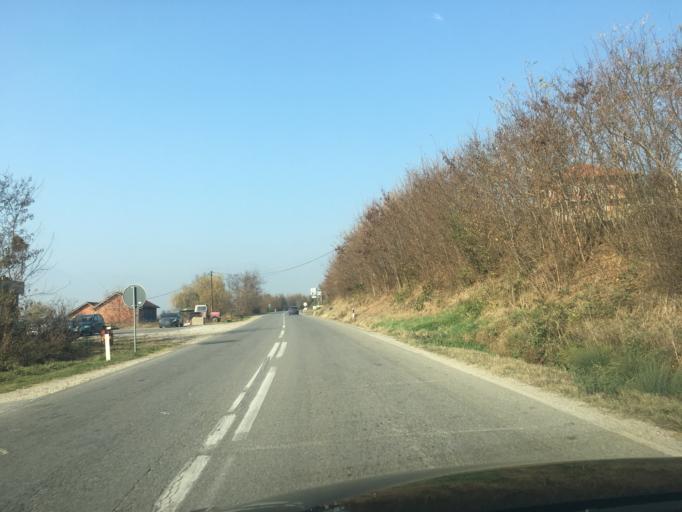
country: XK
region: Pec
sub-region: Komuna e Pejes
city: Dubova (Driloni)
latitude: 42.6429
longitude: 20.4175
